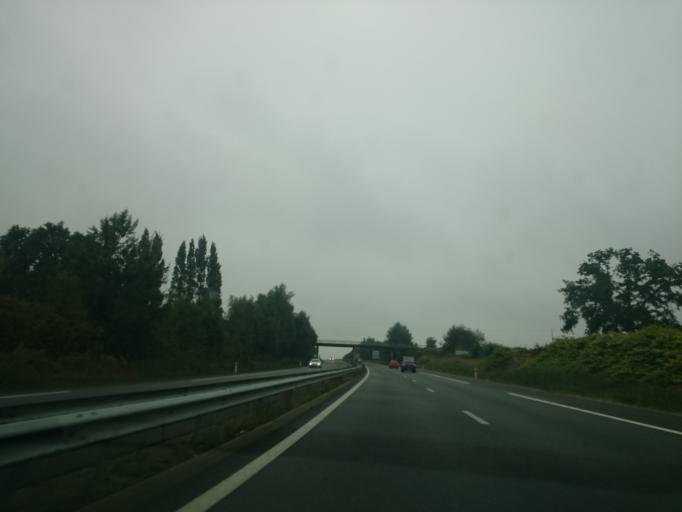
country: FR
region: Brittany
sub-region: Departement d'Ille-et-Vilaine
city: La Dominelais
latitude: 47.7551
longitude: -1.7147
